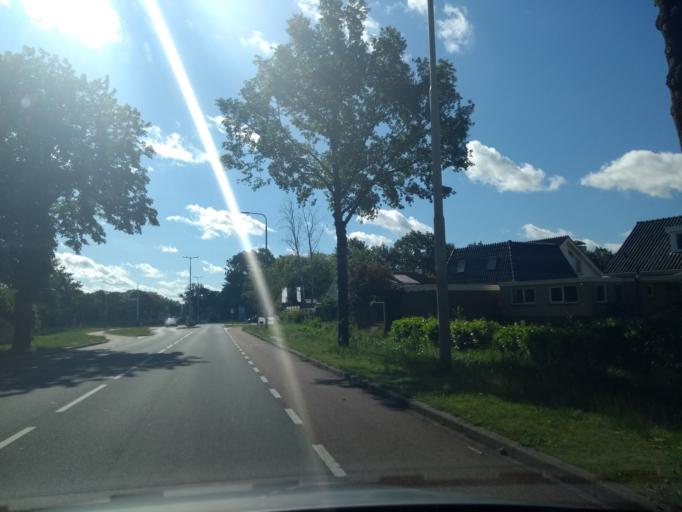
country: DE
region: Lower Saxony
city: Lage
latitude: 52.3960
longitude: 6.9662
